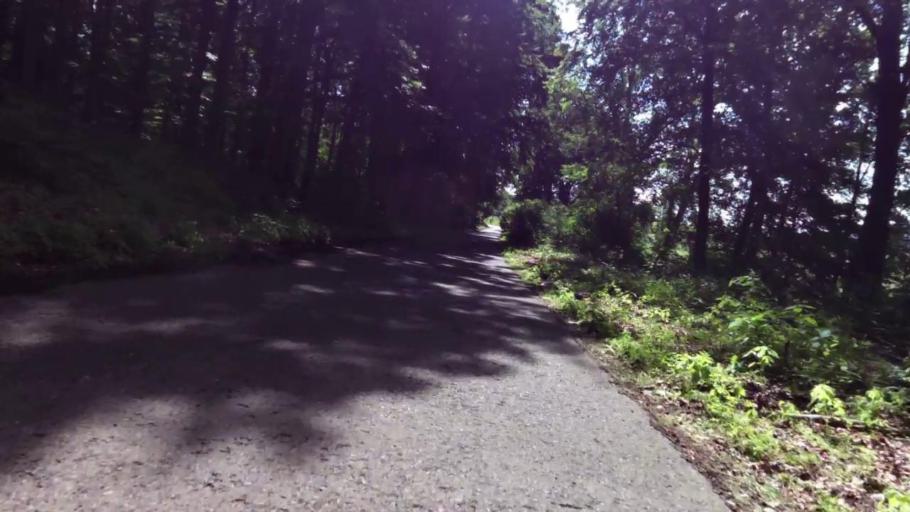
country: PL
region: West Pomeranian Voivodeship
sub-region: Powiat stargardzki
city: Dobrzany
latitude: 53.3907
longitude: 15.4863
